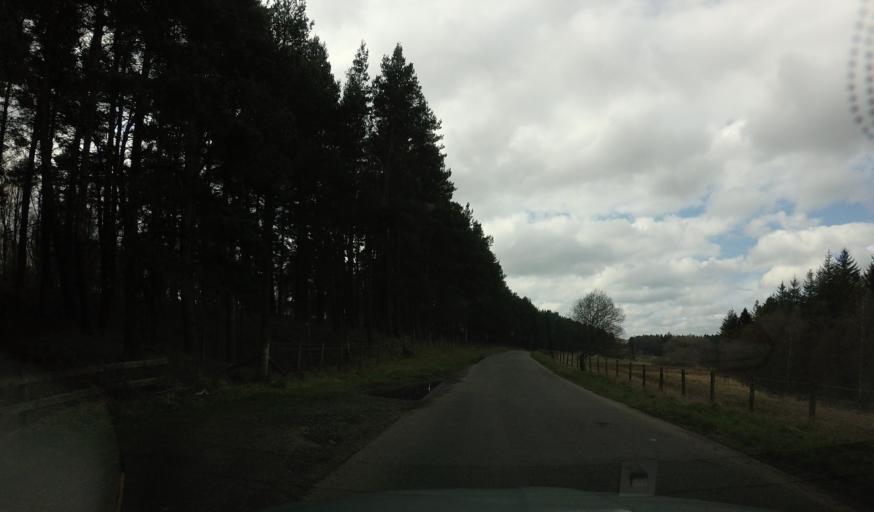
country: GB
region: Scotland
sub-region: Midlothian
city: Bonnyrigg
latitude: 55.7705
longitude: -3.1359
